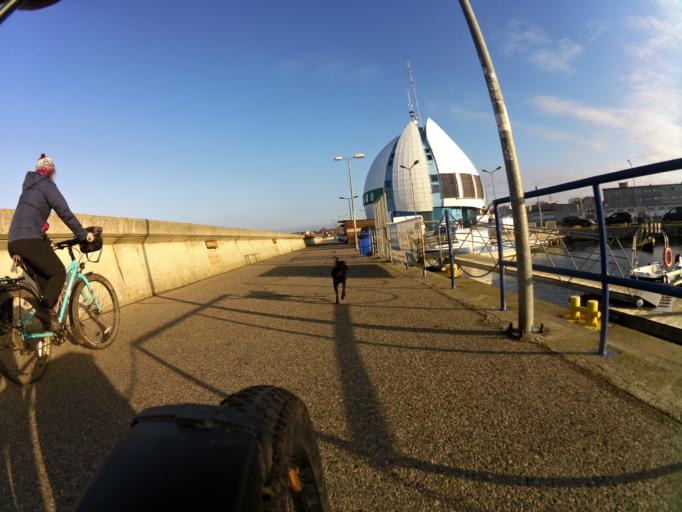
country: PL
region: Pomeranian Voivodeship
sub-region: Powiat pucki
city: Hel
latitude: 54.6027
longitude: 18.7999
